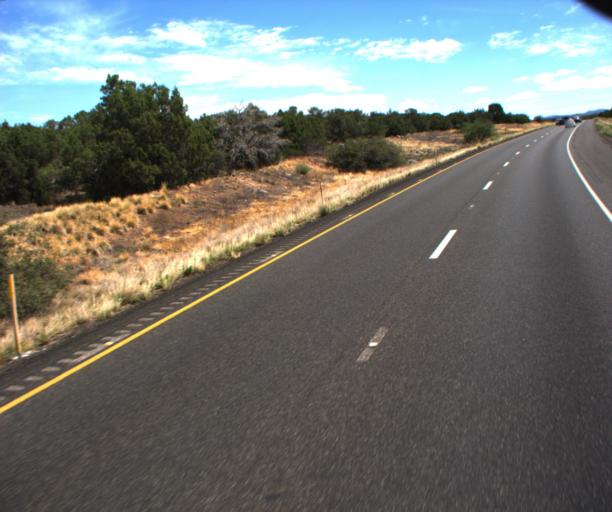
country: US
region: Arizona
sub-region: Yavapai County
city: Big Park
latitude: 34.7300
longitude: -111.7054
